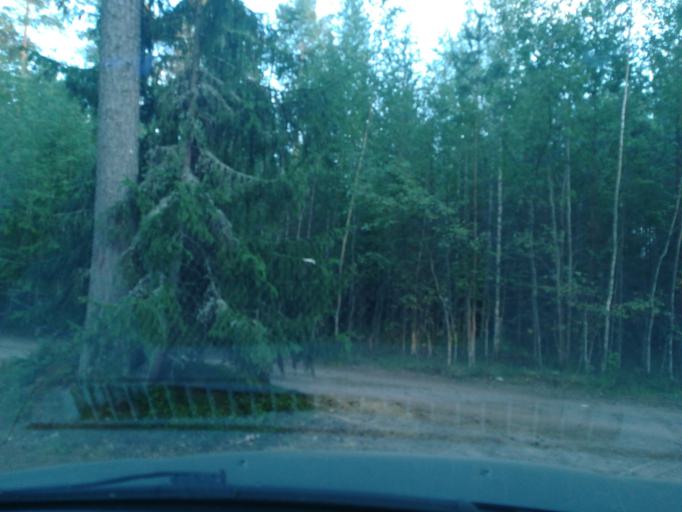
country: RU
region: Leningrad
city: Ust'-Luga
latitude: 59.6783
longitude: 28.2368
